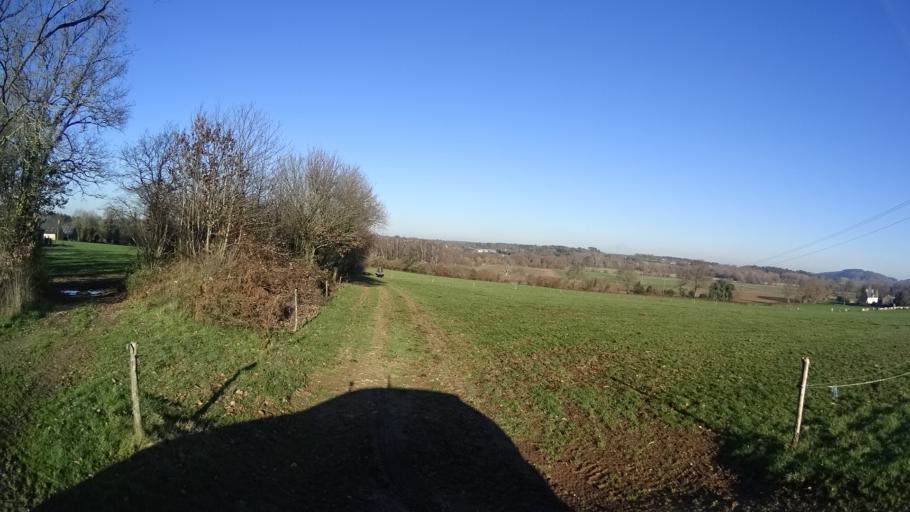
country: FR
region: Brittany
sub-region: Departement du Morbihan
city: Saint-Jean-la-Poterie
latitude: 47.6597
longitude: -2.1318
